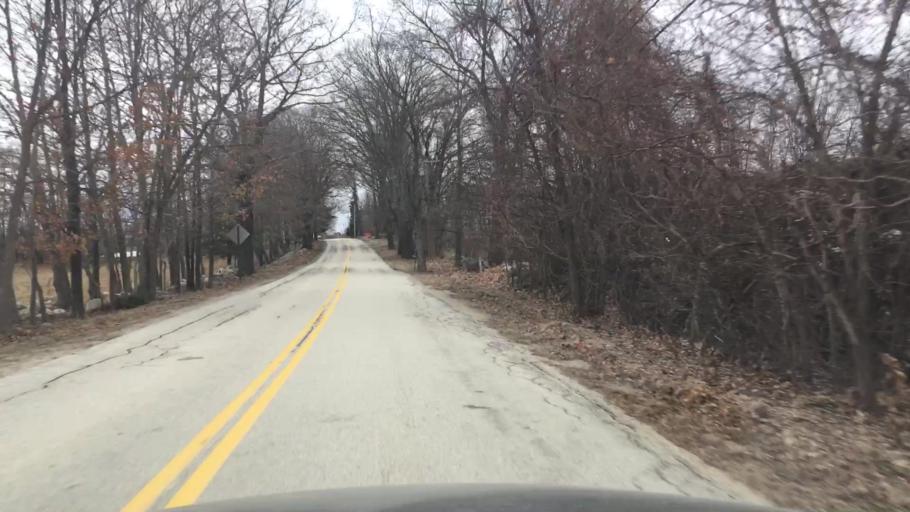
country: US
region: New Hampshire
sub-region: Hillsborough County
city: Mont Vernon
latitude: 42.9244
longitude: -71.6043
